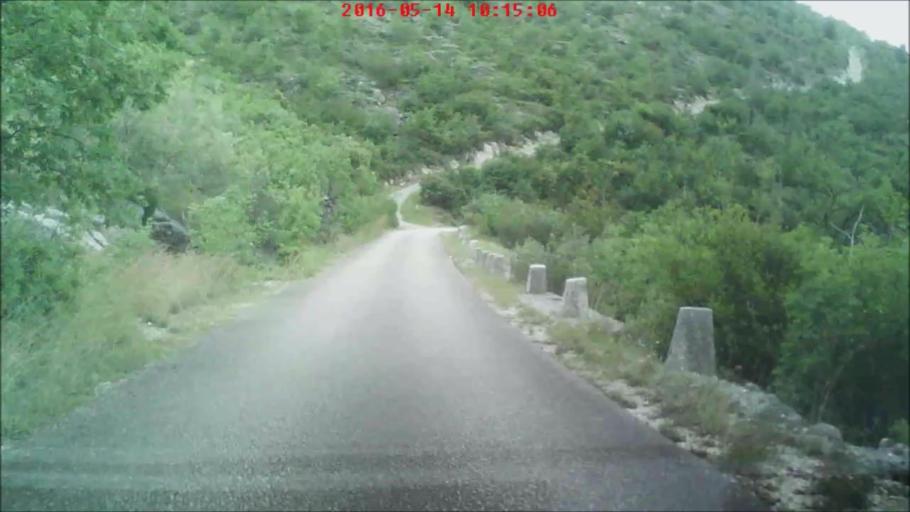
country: HR
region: Dubrovacko-Neretvanska
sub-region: Grad Dubrovnik
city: Mokosica
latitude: 42.7317
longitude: 17.9624
